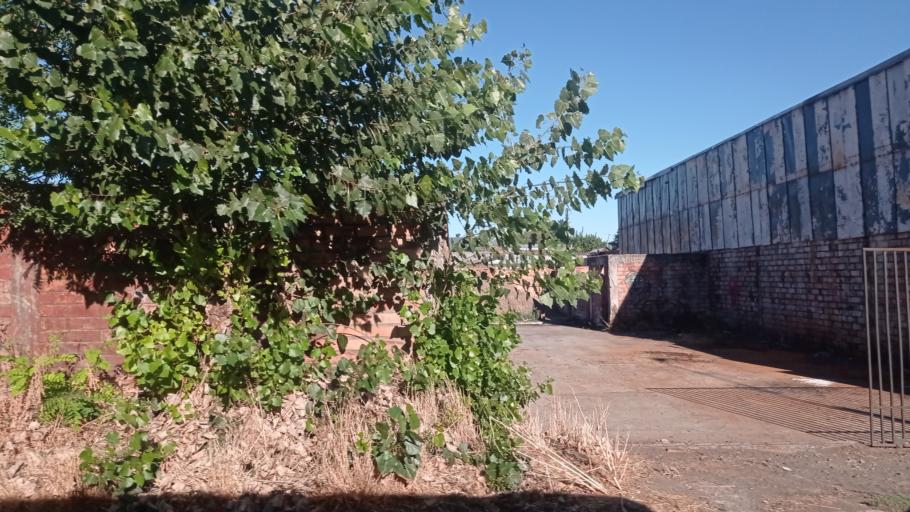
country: CL
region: Biobio
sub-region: Provincia de Biobio
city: Nacimiento
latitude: -37.5095
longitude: -72.6593
